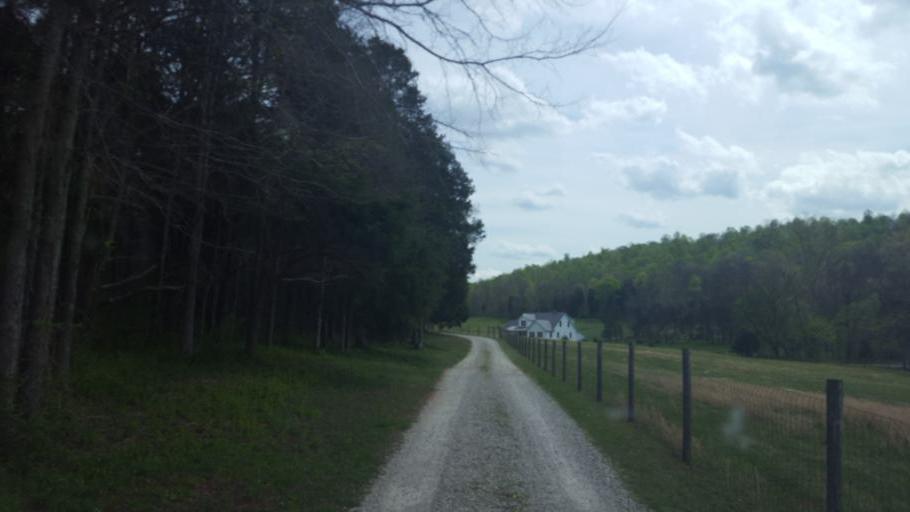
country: US
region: Kentucky
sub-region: Hart County
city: Munfordville
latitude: 37.2506
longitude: -85.9807
